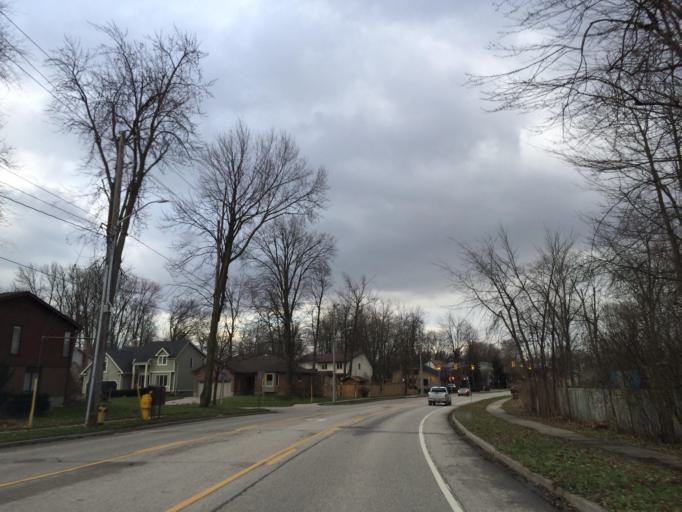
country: CA
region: Ontario
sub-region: Wellington County
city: Guelph
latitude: 43.5359
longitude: -80.2954
